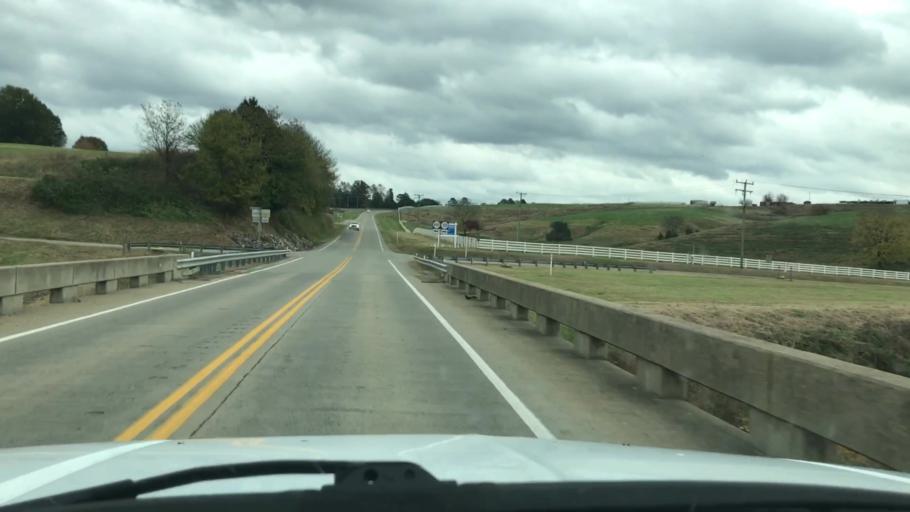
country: US
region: Virginia
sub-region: Goochland County
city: Goochland
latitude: 37.6474
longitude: -77.8258
